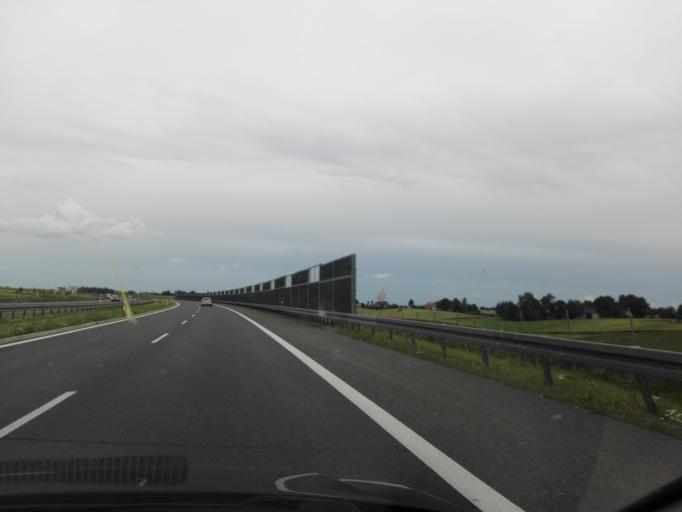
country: PL
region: Lublin Voivodeship
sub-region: Powiat lubelski
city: Jastkow
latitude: 51.2937
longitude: 22.4119
